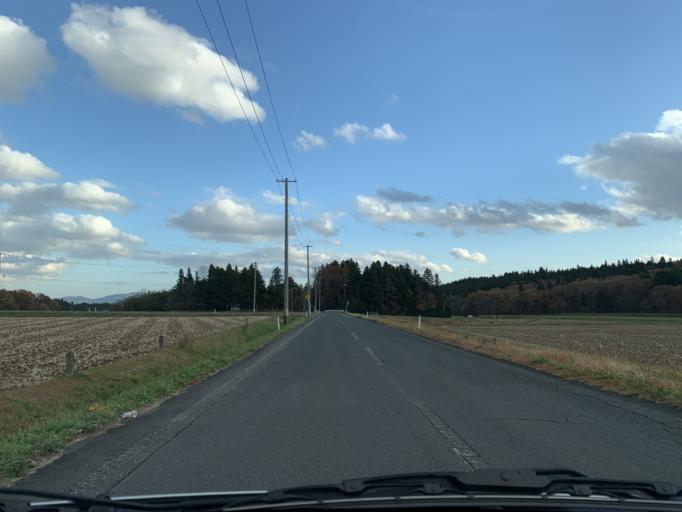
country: JP
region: Iwate
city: Mizusawa
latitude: 39.0941
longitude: 141.0105
